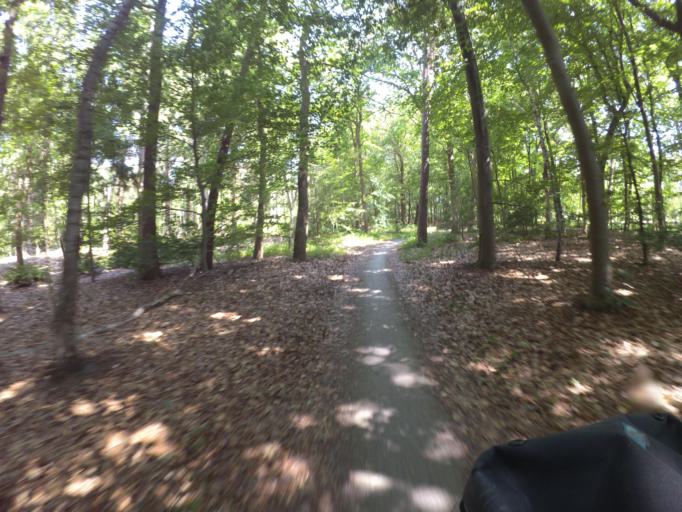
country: NL
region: Drenthe
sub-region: Gemeente De Wolden
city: Ruinen
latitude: 52.7335
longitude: 6.3891
